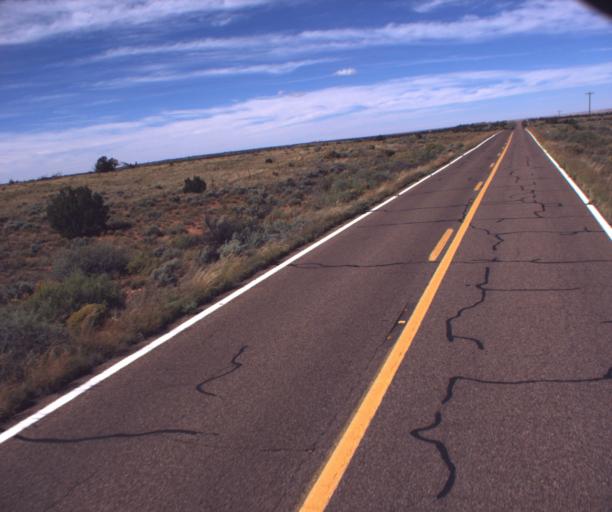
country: US
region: Arizona
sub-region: Apache County
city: Saint Johns
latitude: 34.5678
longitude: -109.6331
